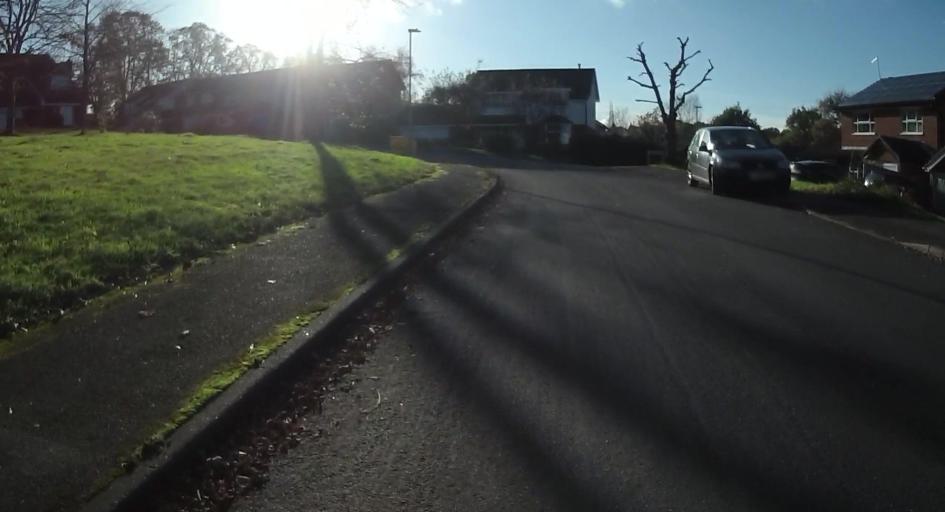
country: GB
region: England
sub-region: Wokingham
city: Wokingham
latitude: 51.4064
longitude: -0.8562
